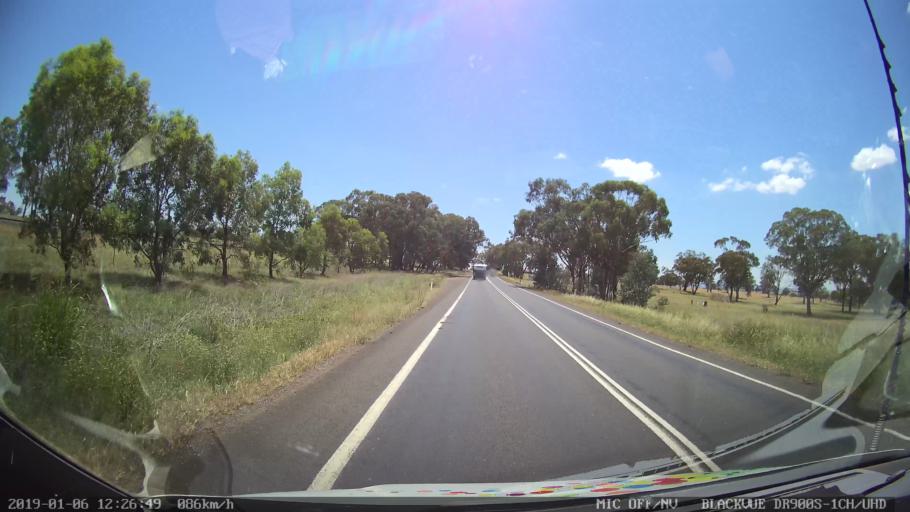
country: AU
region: New South Wales
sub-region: Tamworth Municipality
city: Phillip
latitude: -31.2138
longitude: 150.8227
